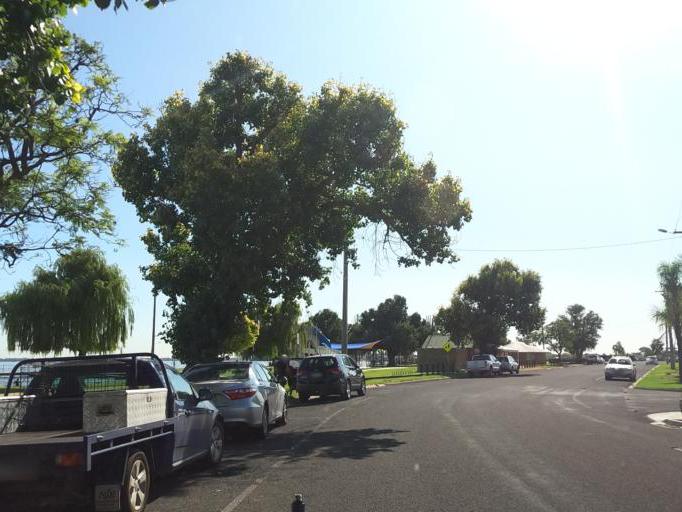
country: AU
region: Victoria
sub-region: Moira
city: Yarrawonga
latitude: -36.0069
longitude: 146.0097
